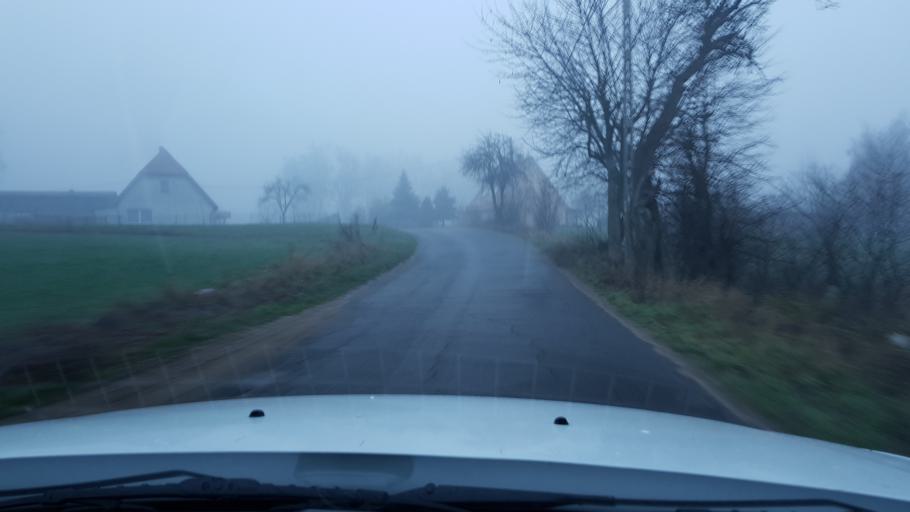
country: PL
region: West Pomeranian Voivodeship
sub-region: Powiat mysliborski
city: Mysliborz
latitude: 52.9020
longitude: 14.8226
